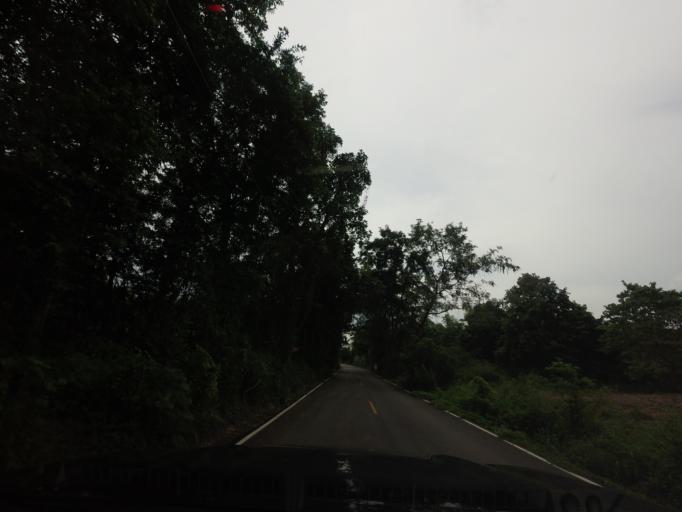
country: TH
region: Changwat Nong Bua Lamphu
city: Nong Bua Lamphu
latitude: 17.2534
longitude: 102.3858
